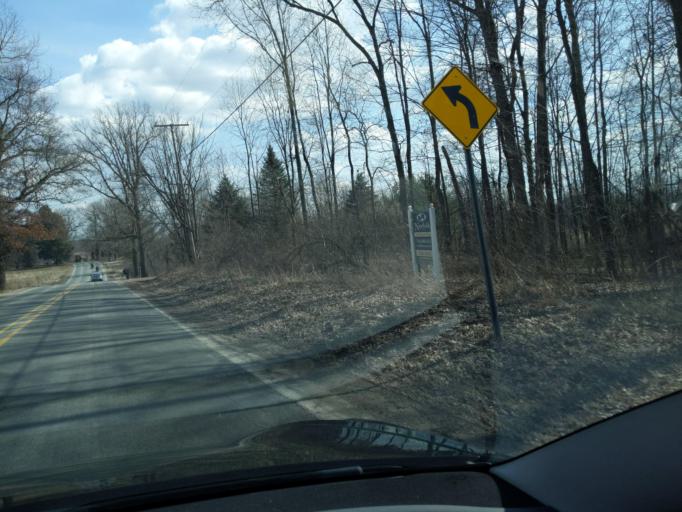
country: US
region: Michigan
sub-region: Livingston County
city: Pinckney
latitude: 42.3917
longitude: -83.9582
